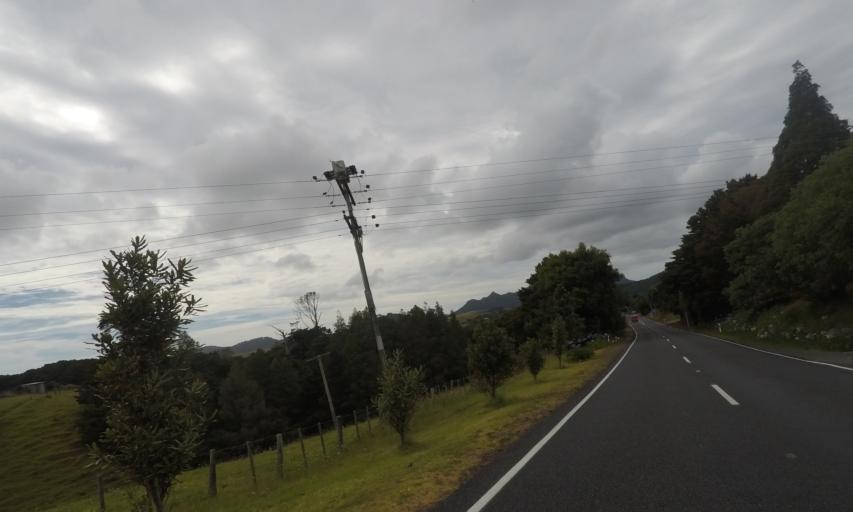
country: NZ
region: Northland
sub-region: Whangarei
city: Ruakaka
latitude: -35.7647
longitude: 174.4739
